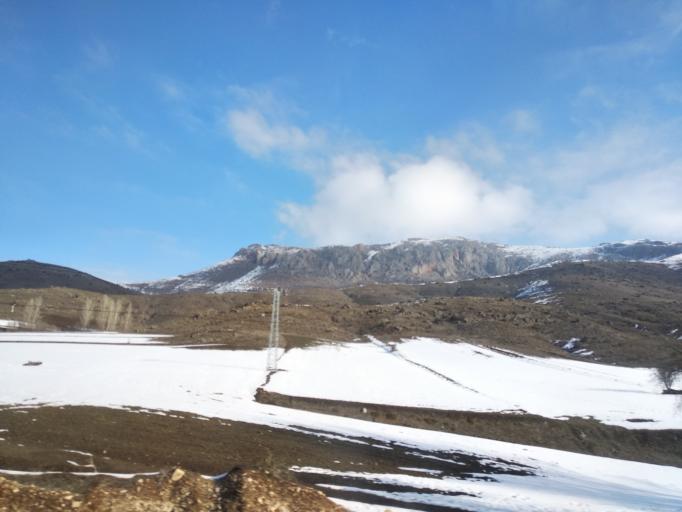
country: TR
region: Gumushane
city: Kelkit
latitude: 40.0127
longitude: 39.5332
